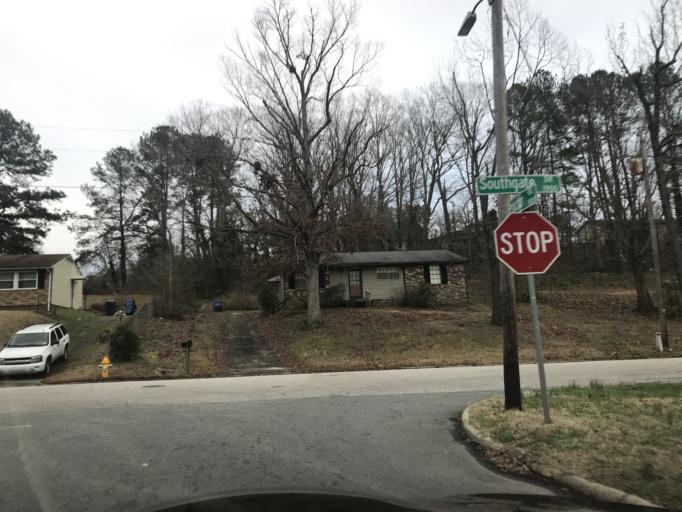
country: US
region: North Carolina
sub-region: Wake County
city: Raleigh
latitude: 35.7529
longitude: -78.6087
